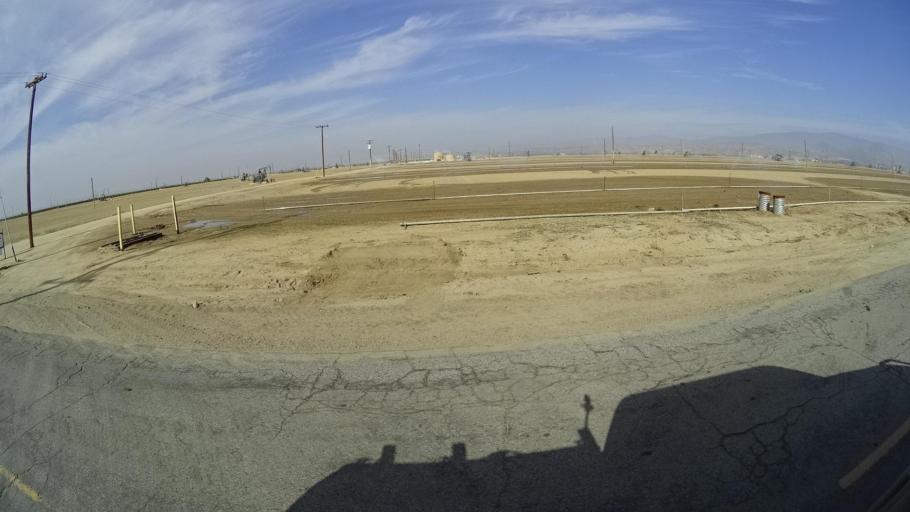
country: US
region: California
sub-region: Kern County
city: Lamont
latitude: 35.3110
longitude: -118.8299
